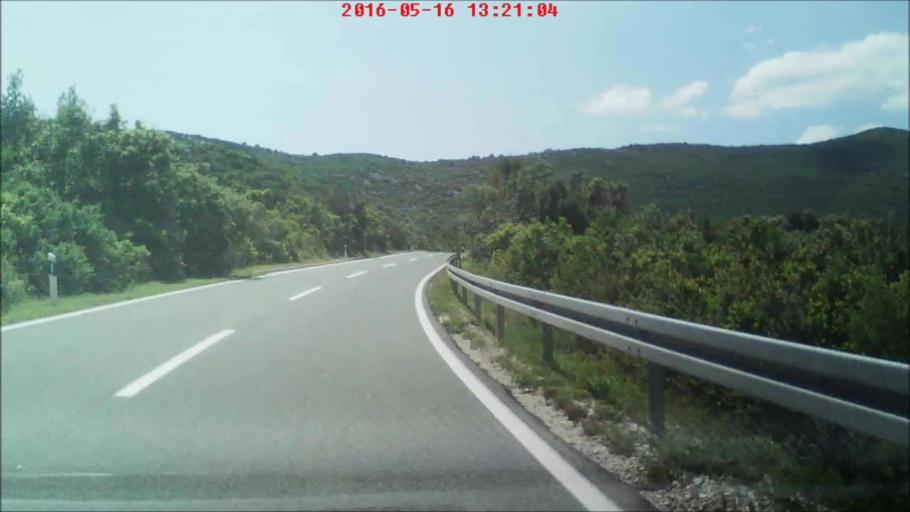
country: HR
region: Dubrovacko-Neretvanska
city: Ston
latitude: 42.8319
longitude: 17.7375
